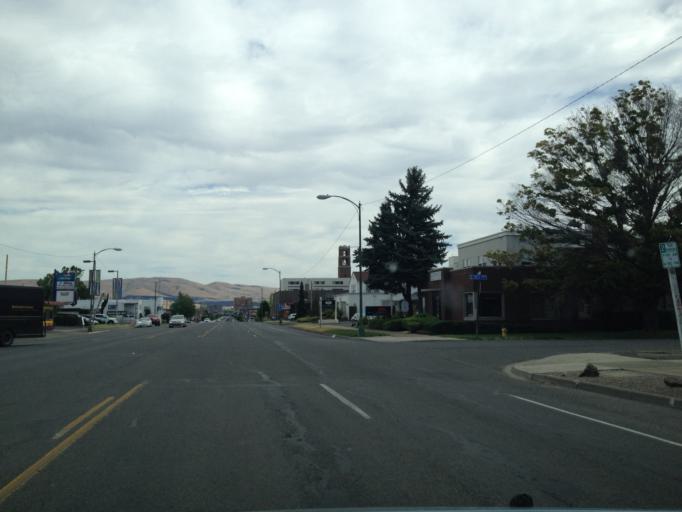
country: US
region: Washington
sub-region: Yakima County
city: Yakima
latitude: 46.5982
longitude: -120.5235
